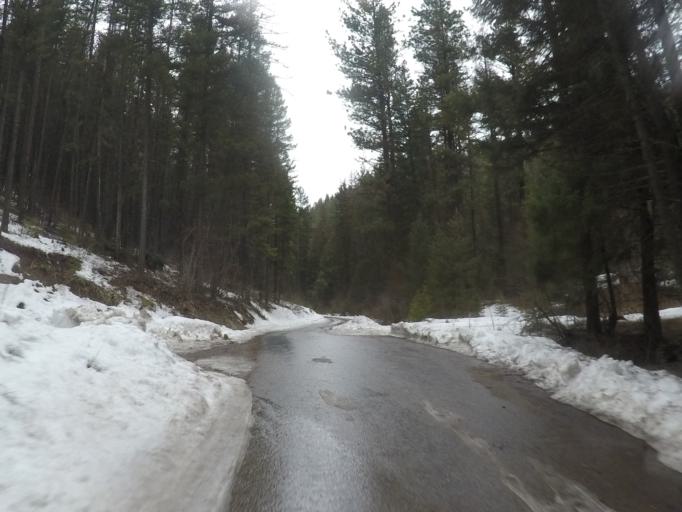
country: US
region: Montana
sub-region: Missoula County
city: East Missoula
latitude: 46.9285
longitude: -113.9672
